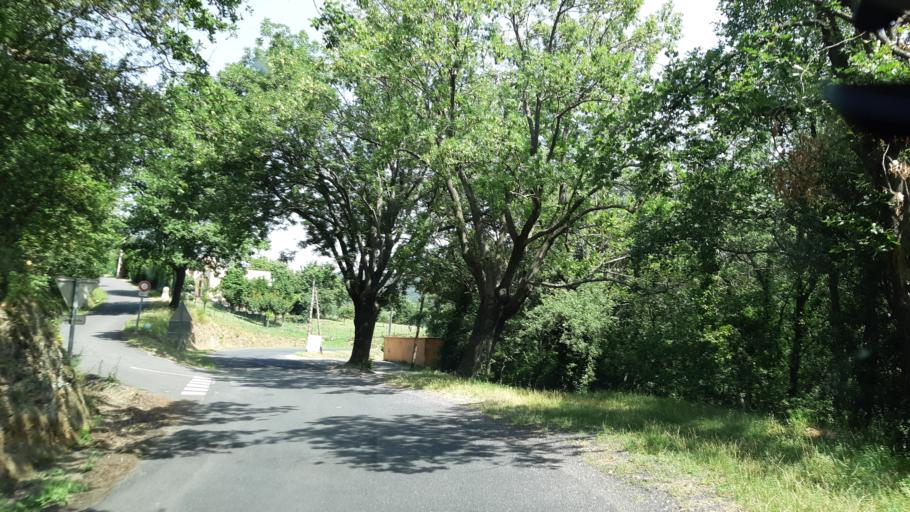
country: FR
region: Languedoc-Roussillon
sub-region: Departement des Pyrenees-Orientales
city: els Banys d'Arles
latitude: 42.5211
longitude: 2.6343
